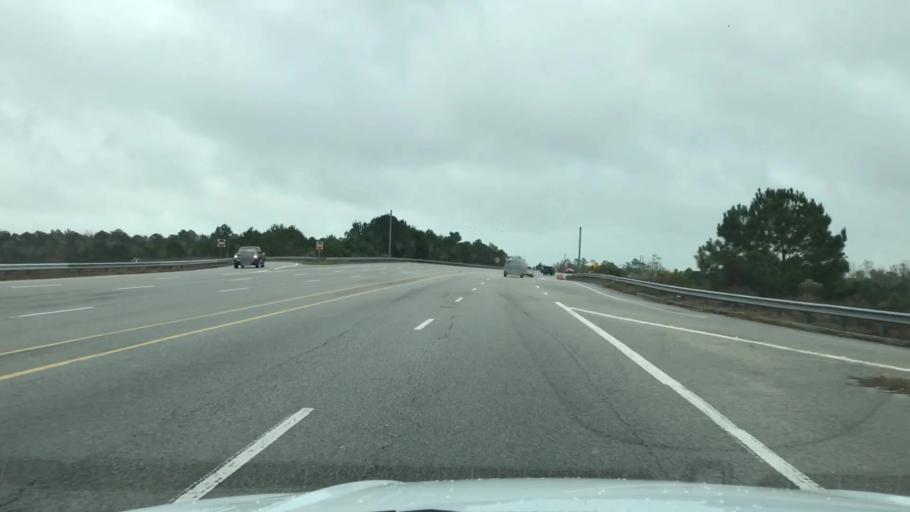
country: US
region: South Carolina
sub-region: Horry County
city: Myrtle Beach
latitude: 33.7559
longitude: -78.8546
